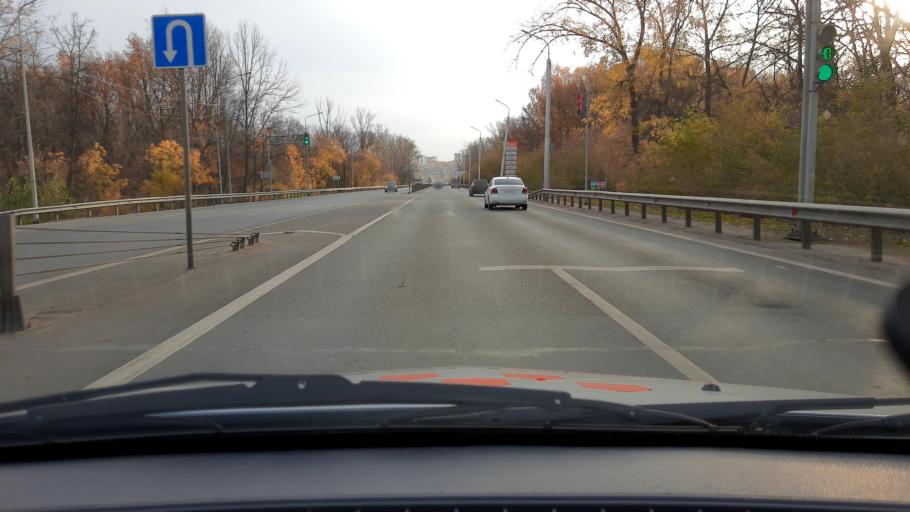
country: RU
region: Bashkortostan
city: Ufa
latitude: 54.7002
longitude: 55.9285
